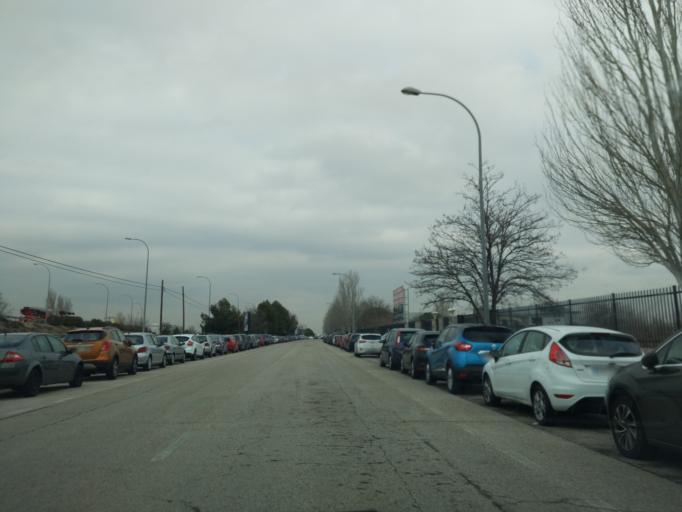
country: ES
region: Madrid
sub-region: Provincia de Madrid
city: Torrejon de Ardoz
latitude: 40.4572
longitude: -3.5019
